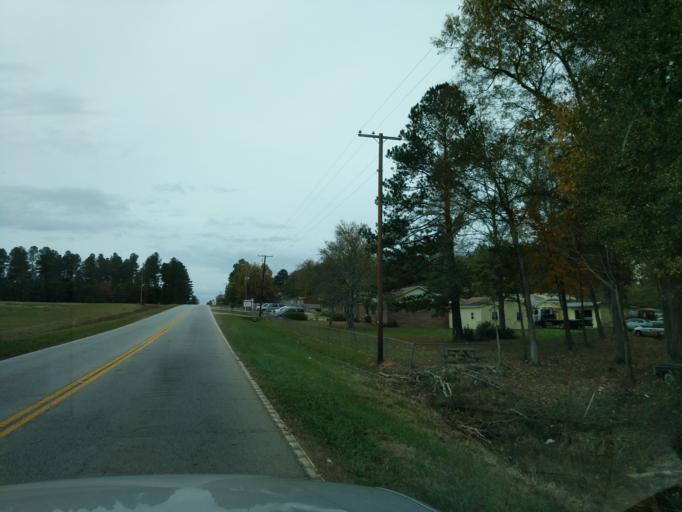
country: US
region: South Carolina
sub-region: Saluda County
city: Saluda
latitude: 34.0746
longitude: -81.7592
